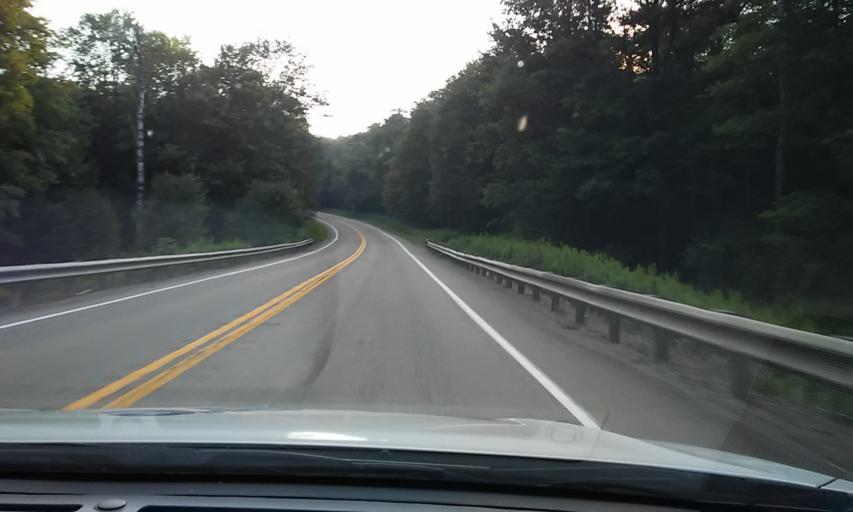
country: US
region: Pennsylvania
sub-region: Forest County
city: Marienville
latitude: 41.5500
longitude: -79.0179
